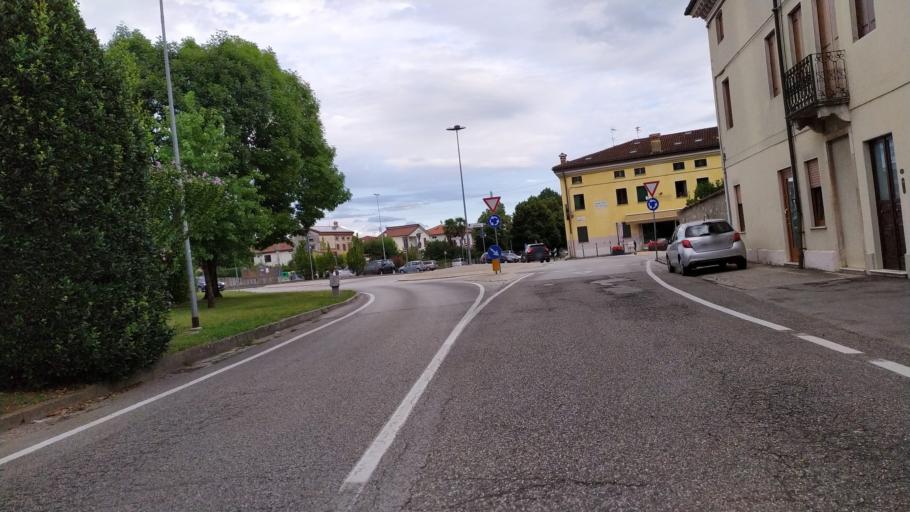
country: IT
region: Veneto
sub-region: Provincia di Vicenza
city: Malo
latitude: 45.6579
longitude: 11.4121
